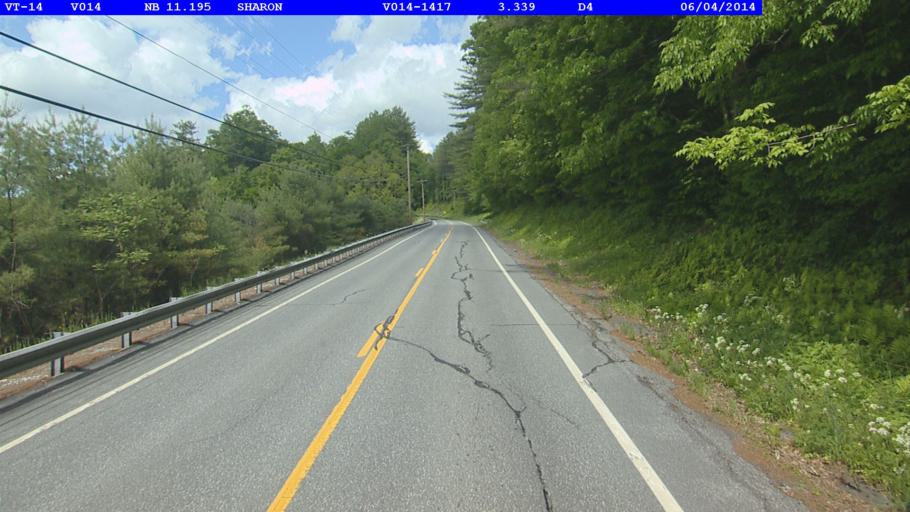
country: US
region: Vermont
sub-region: Windsor County
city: Woodstock
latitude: 43.7641
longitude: -72.4477
